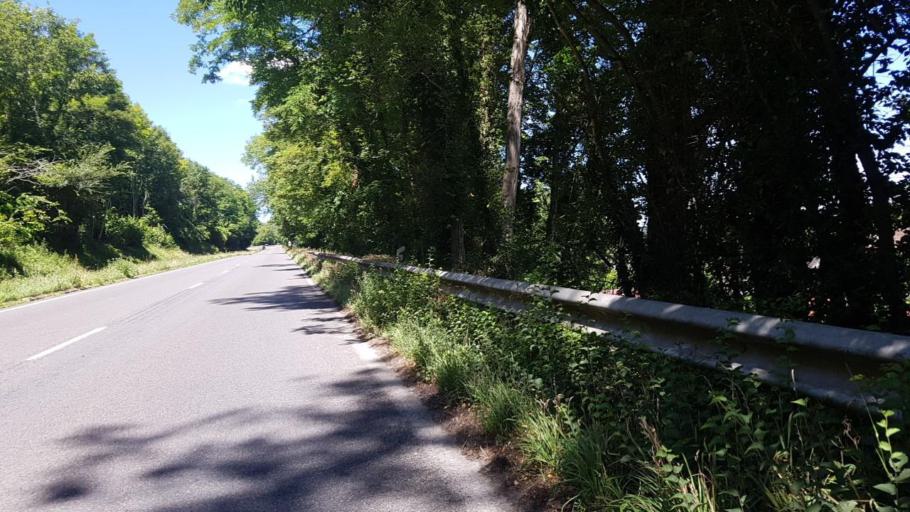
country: FR
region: Ile-de-France
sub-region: Departement de Seine-et-Marne
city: Saint-Jean-les-Deux-Jumeaux
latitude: 48.9557
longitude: 3.0051
